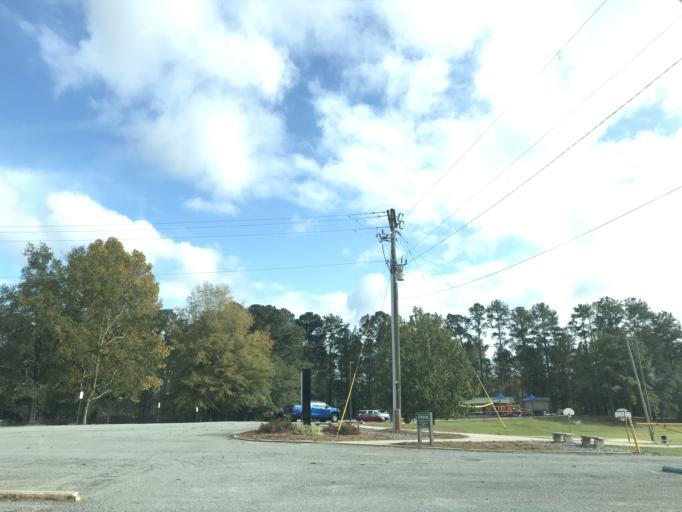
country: US
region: Georgia
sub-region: Jones County
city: Gray
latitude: 32.9850
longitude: -83.5188
